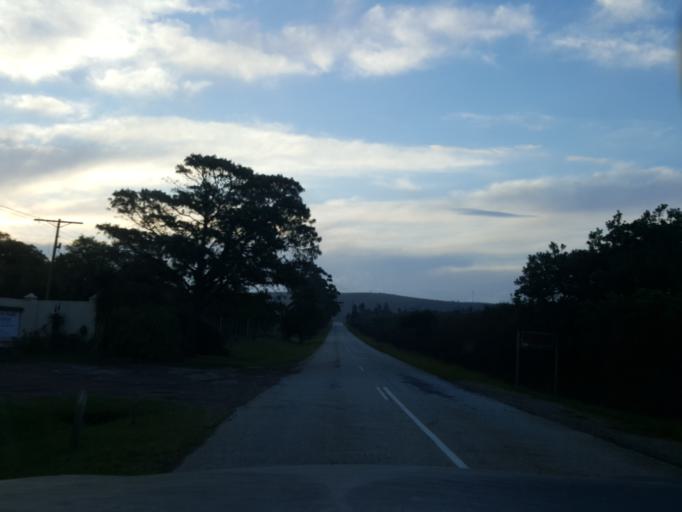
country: ZA
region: Eastern Cape
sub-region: Cacadu District Municipality
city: Grahamstown
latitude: -33.3877
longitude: 26.4730
